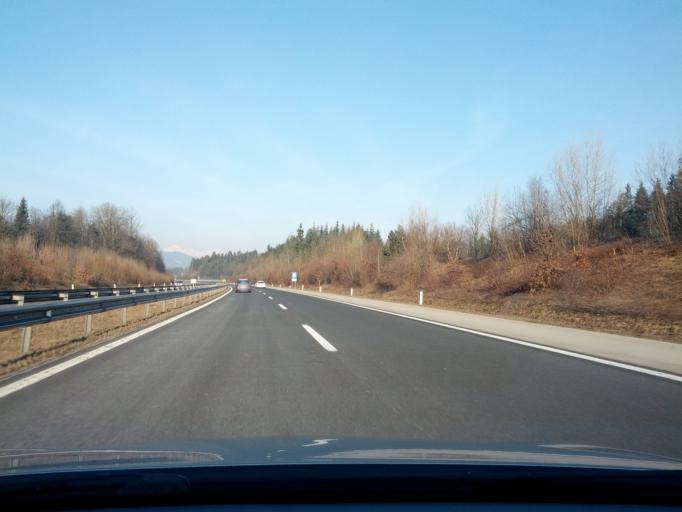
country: SI
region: Kranj
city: Britof
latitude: 46.2583
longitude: 14.3751
